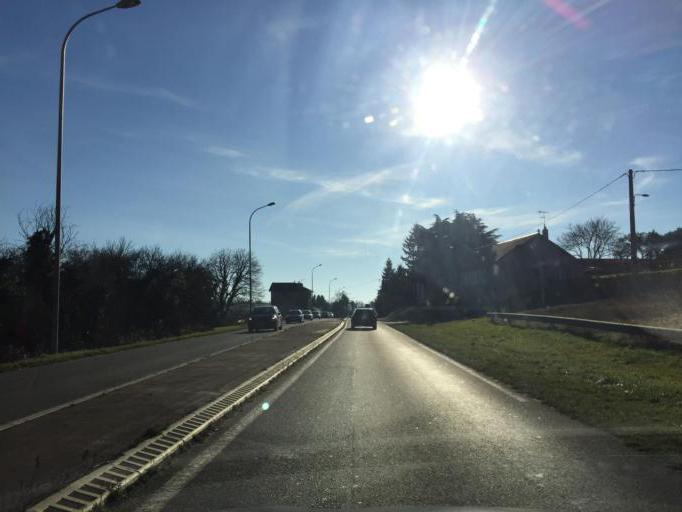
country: FR
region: Auvergne
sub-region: Departement de l'Allier
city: Bellerive-sur-Allier
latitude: 46.1485
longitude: 3.3946
